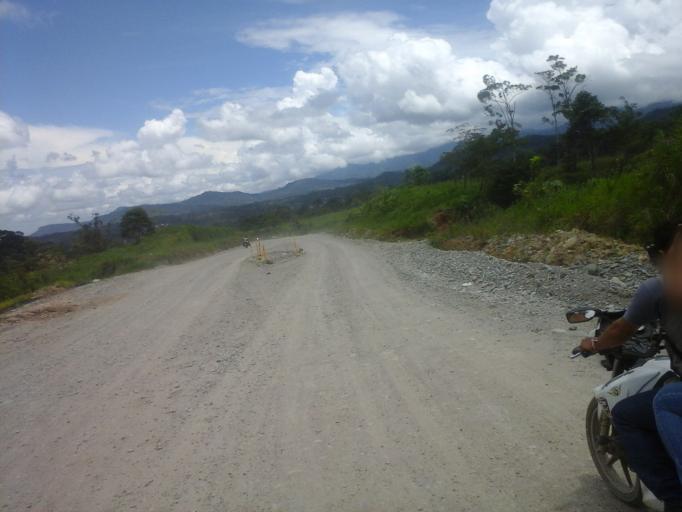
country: CO
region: Putumayo
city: Mocoa
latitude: 1.1708
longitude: -76.6548
